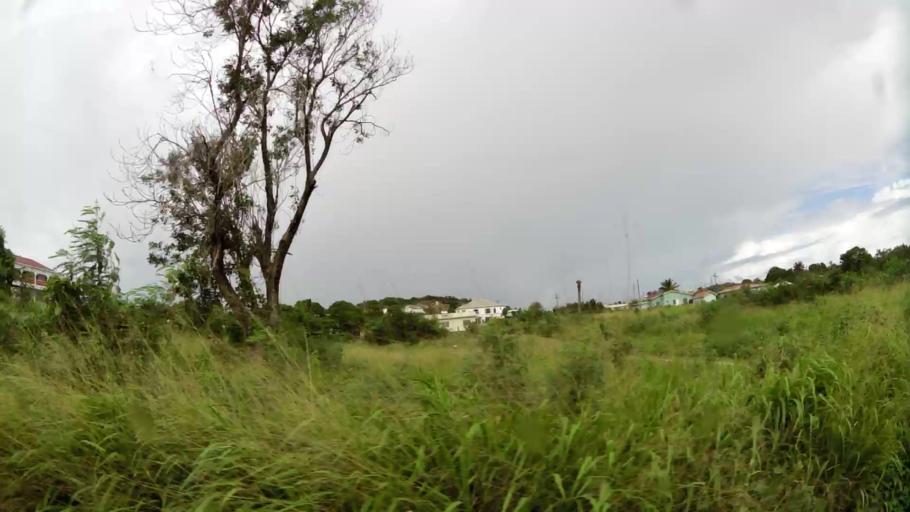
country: AG
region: Saint John
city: Potters Village
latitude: 17.0935
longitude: -61.8189
